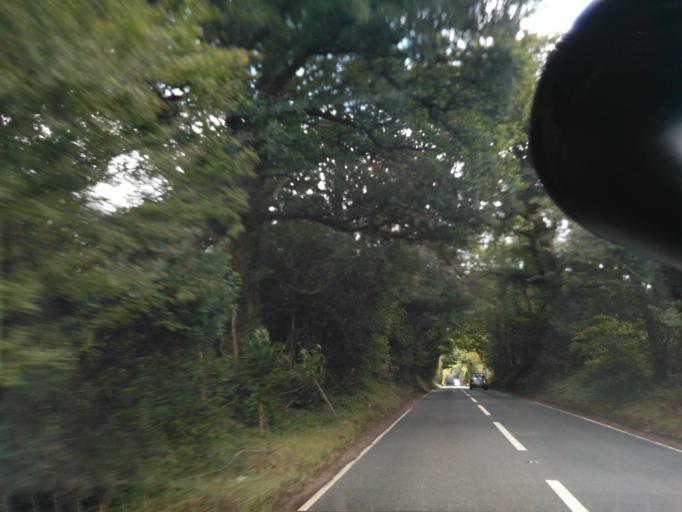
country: GB
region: England
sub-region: Dorset
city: Lytchett Matravers
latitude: 50.7579
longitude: -2.0519
